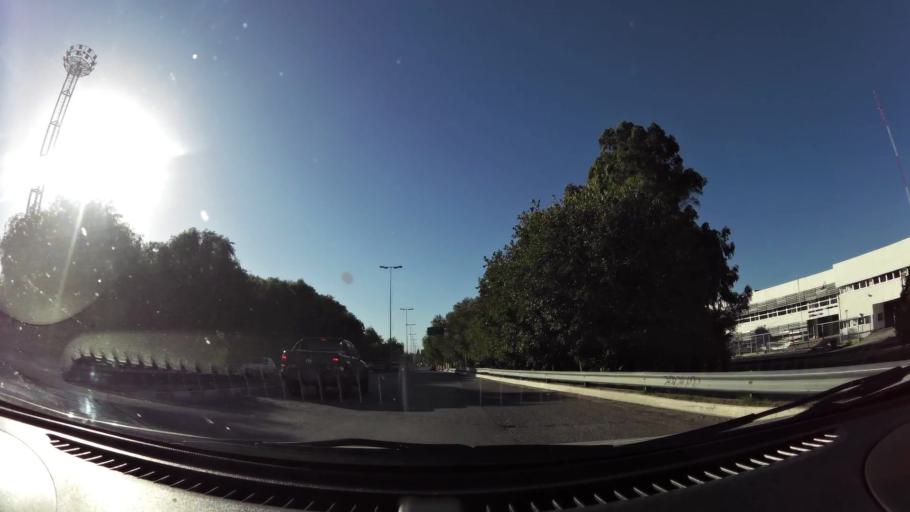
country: AR
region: San Juan
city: Villa Krause
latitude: -31.5547
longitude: -68.5178
